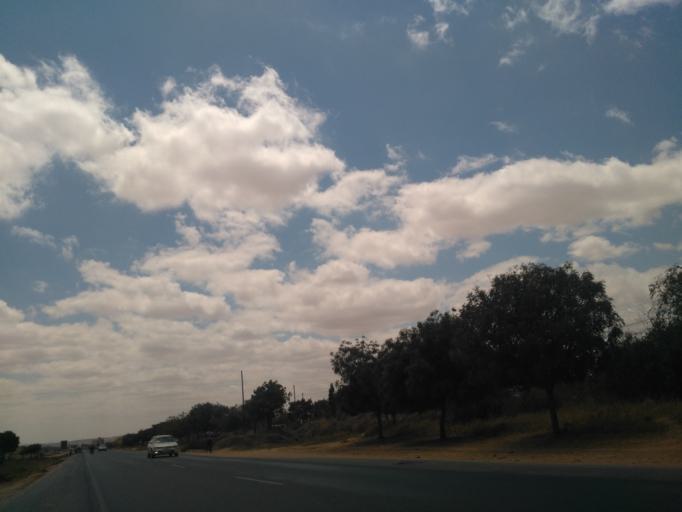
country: TZ
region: Dodoma
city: Kisasa
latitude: -6.1614
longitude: 35.7927
